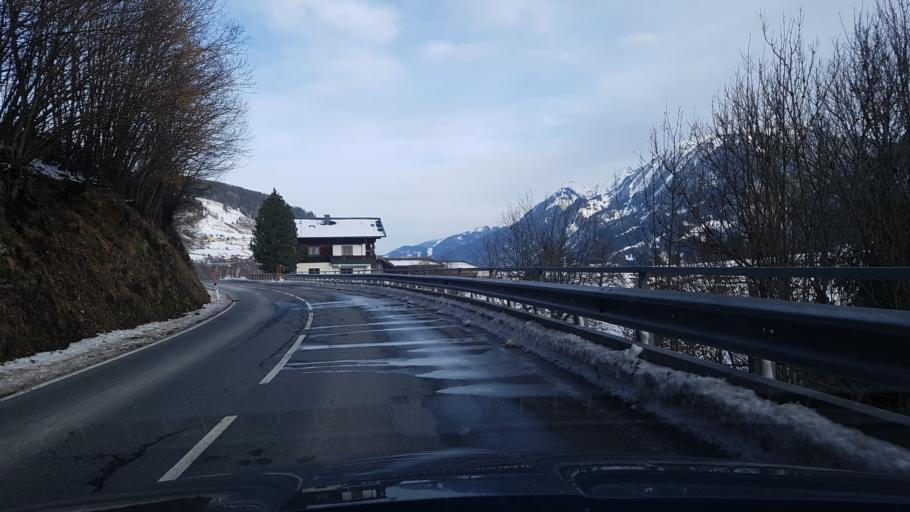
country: AT
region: Salzburg
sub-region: Politischer Bezirk Zell am See
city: Lend
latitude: 47.2968
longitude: 13.0256
